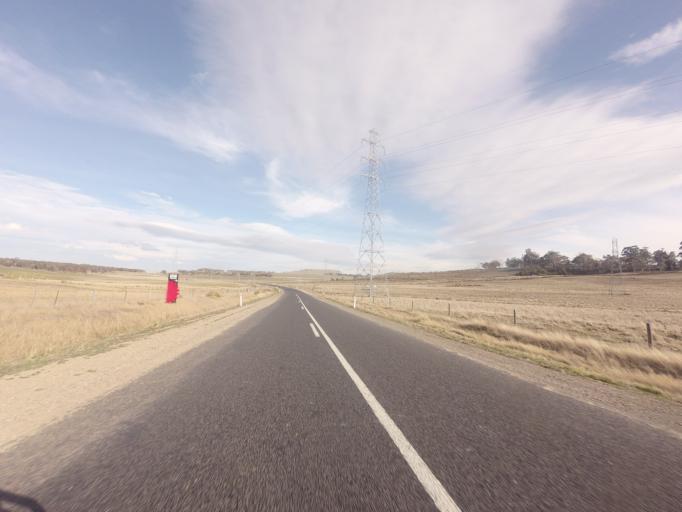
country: AU
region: Tasmania
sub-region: Derwent Valley
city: New Norfolk
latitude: -42.2602
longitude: 146.9377
